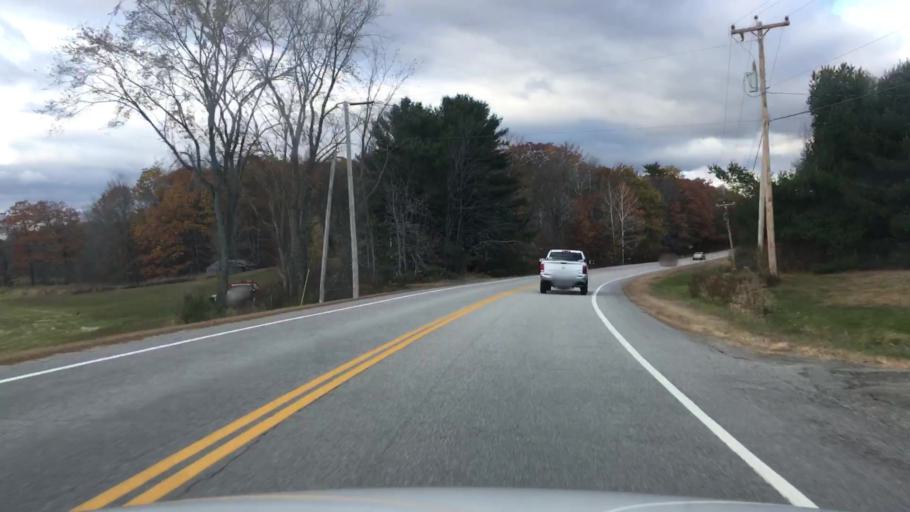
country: US
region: Maine
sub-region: Androscoggin County
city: Leeds
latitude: 44.3378
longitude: -70.1320
